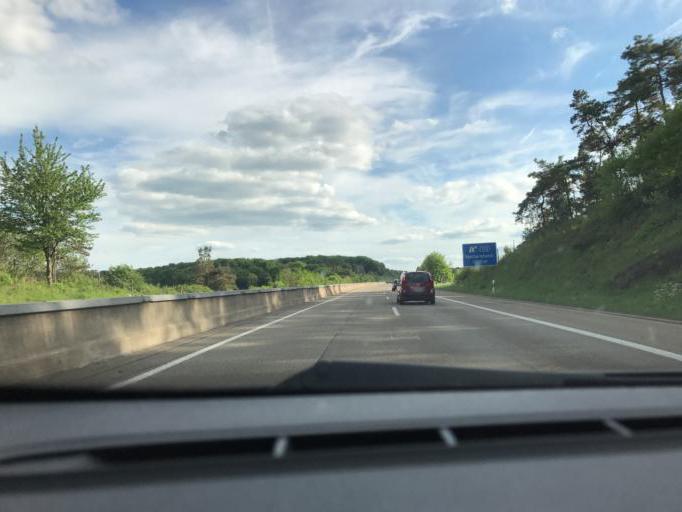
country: DE
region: North Rhine-Westphalia
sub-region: Regierungsbezirk Koln
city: Mechernich
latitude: 50.5403
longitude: 6.6766
